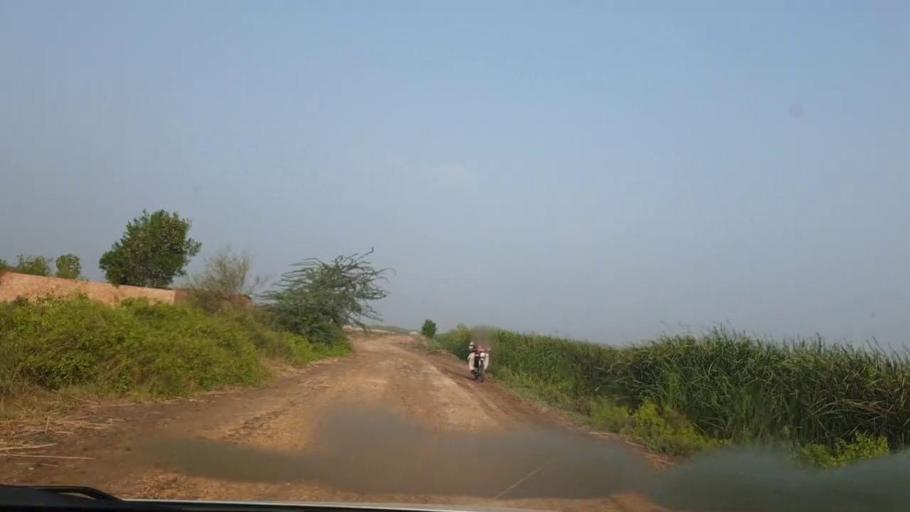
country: PK
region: Sindh
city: Tando Muhammad Khan
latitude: 25.0936
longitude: 68.4780
